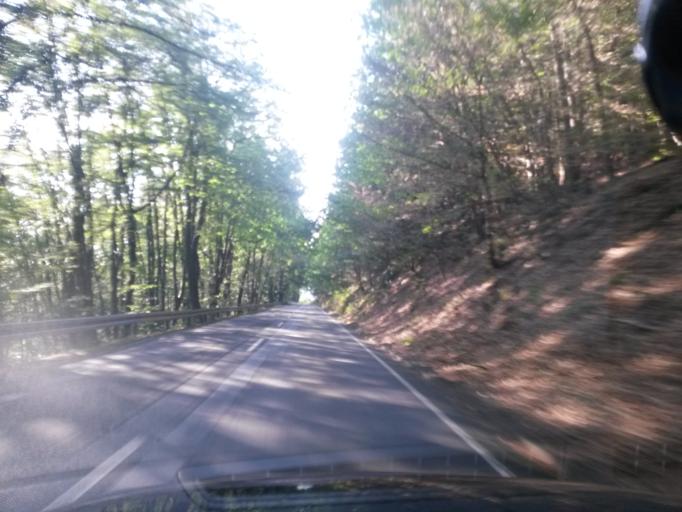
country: DE
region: North Rhine-Westphalia
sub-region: Regierungsbezirk Koln
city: Gummersbach
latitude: 50.9947
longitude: 7.5789
